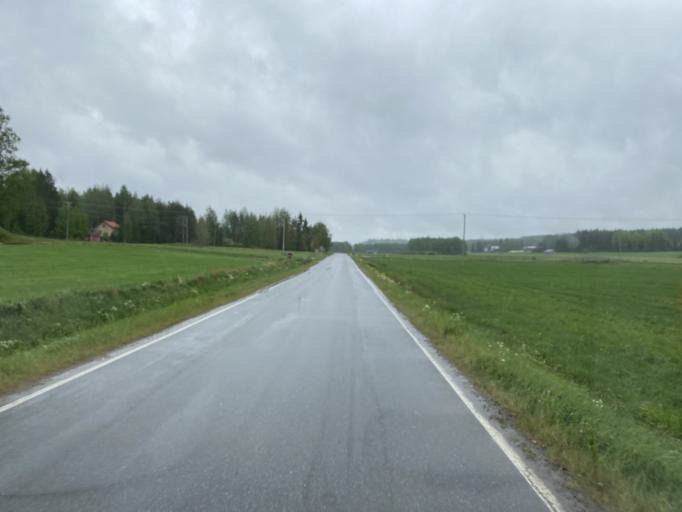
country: FI
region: Haeme
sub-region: Forssa
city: Humppila
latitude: 61.0429
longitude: 23.3917
